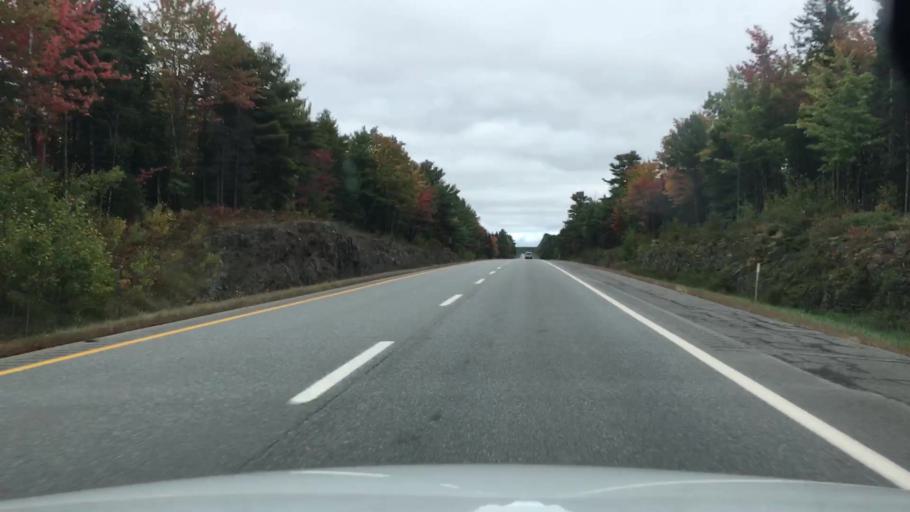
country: US
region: Maine
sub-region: Penobscot County
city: Plymouth
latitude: 44.7889
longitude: -69.1774
